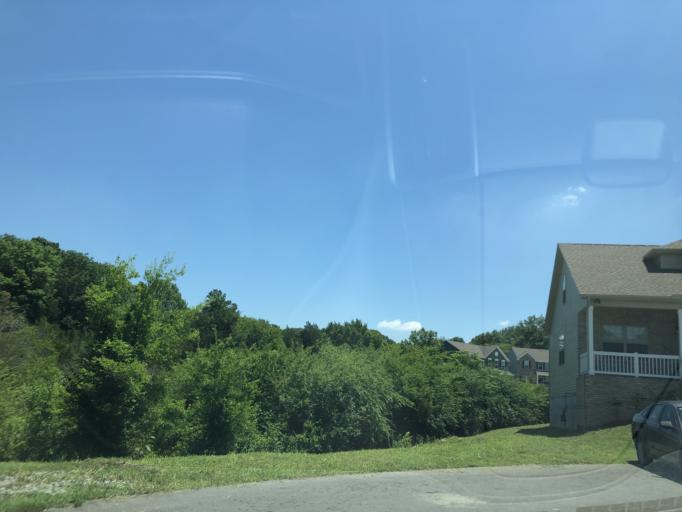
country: US
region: Tennessee
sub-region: Rutherford County
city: La Vergne
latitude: 36.0241
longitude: -86.6502
